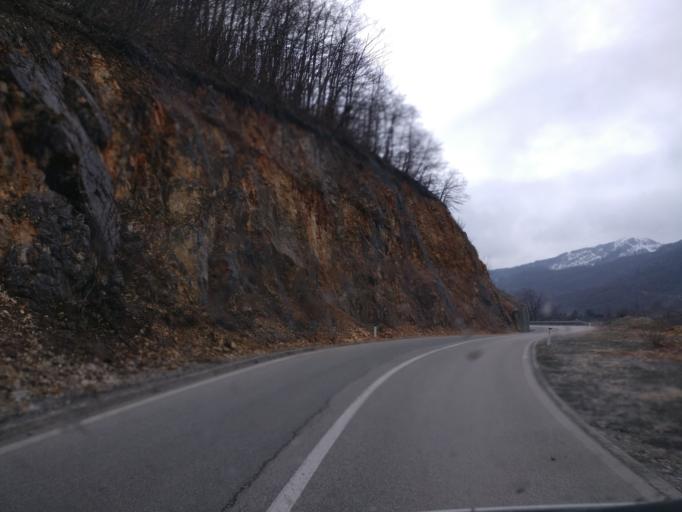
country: ME
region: Opstina Pluzine
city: Pluzine
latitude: 43.1300
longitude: 18.8155
